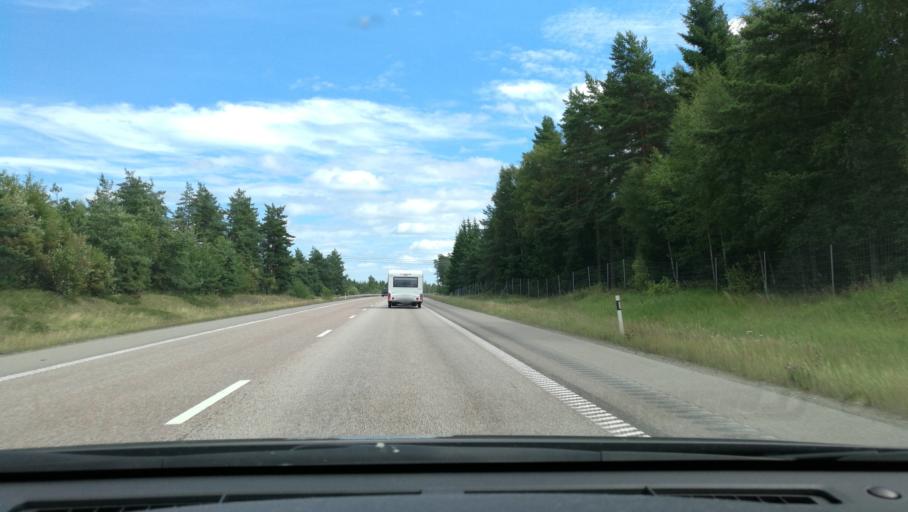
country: SE
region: Uppsala
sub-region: Enkopings Kommun
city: Grillby
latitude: 59.6448
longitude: 17.1894
